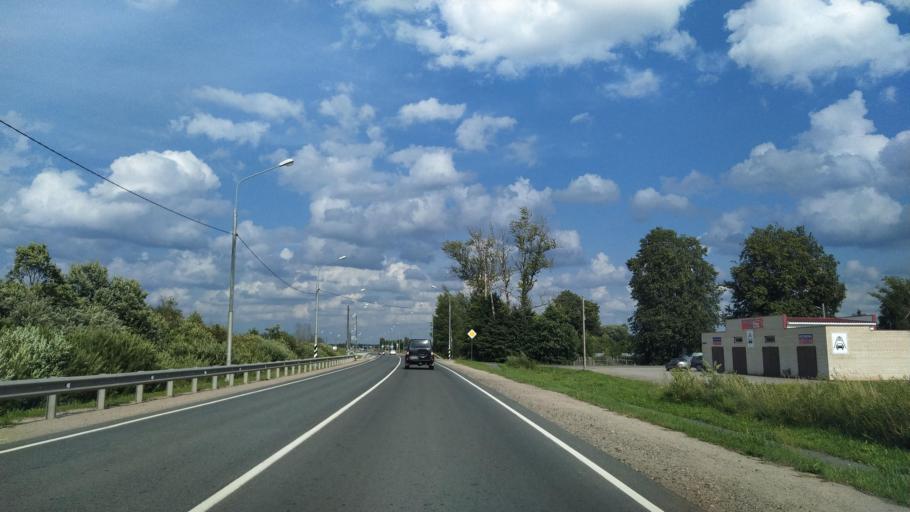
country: RU
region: Novgorod
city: Sol'tsy
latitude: 58.1272
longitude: 30.3527
